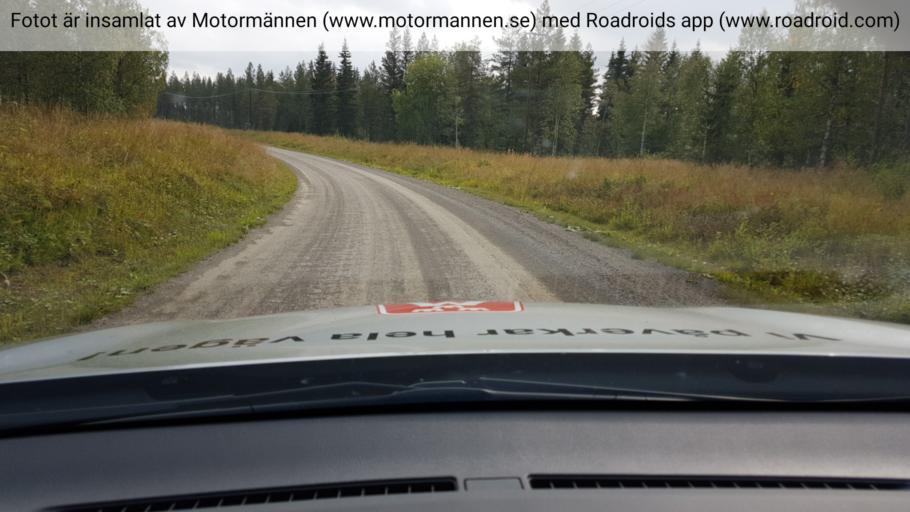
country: SE
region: Jaemtland
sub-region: Stroemsunds Kommun
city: Stroemsund
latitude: 63.7433
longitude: 15.3865
